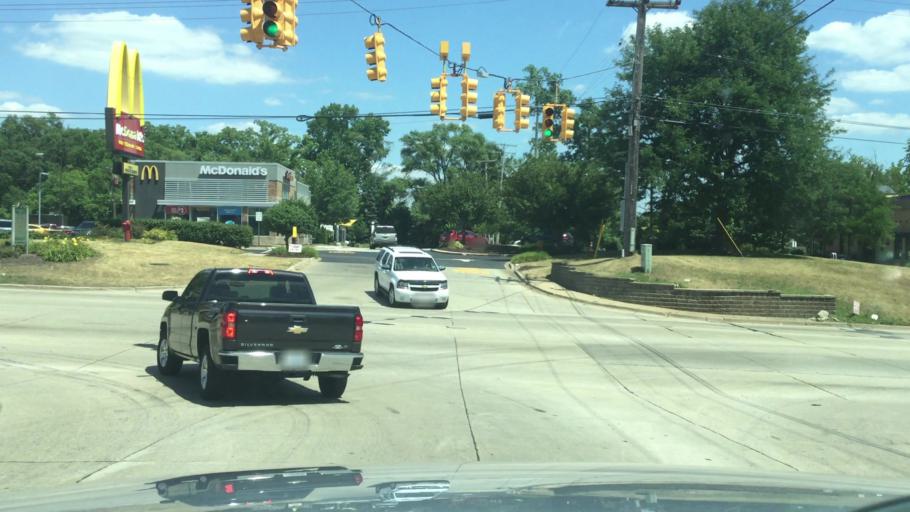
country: US
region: Michigan
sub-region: Wayne County
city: Belleville
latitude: 42.2138
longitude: -83.5439
